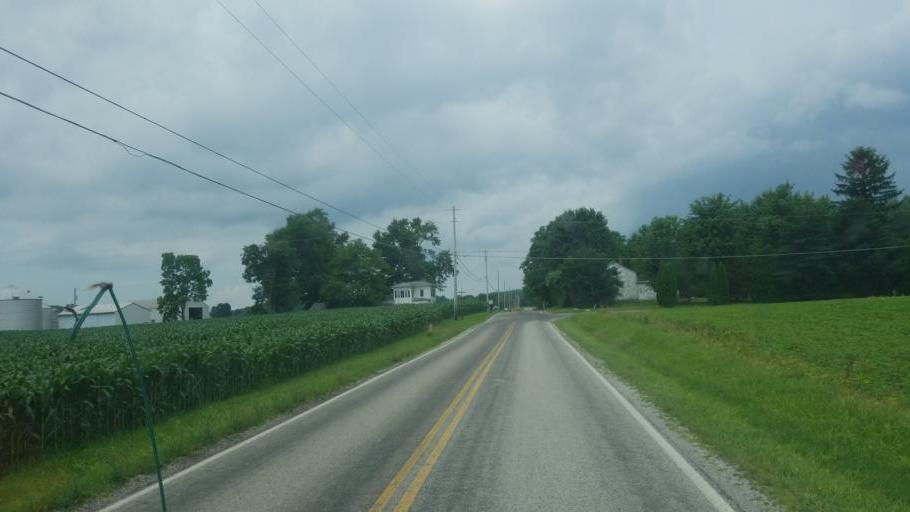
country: US
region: Ohio
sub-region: Wayne County
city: Wooster
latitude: 40.8939
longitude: -81.9534
